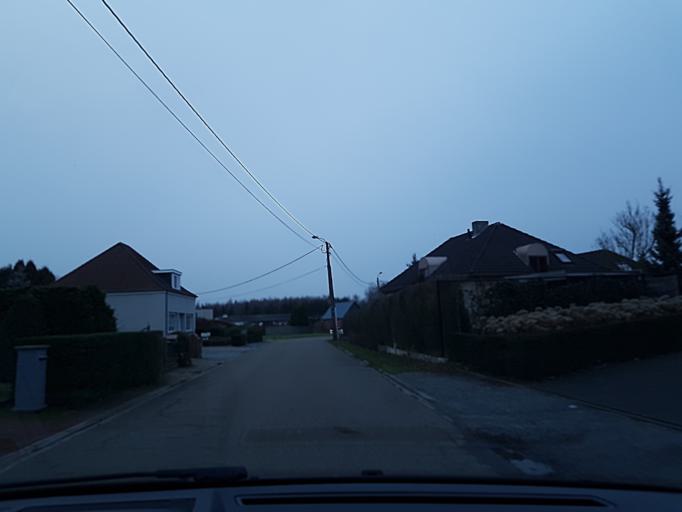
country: BE
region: Flanders
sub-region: Provincie Antwerpen
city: Bonheiden
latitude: 51.0199
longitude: 4.5269
